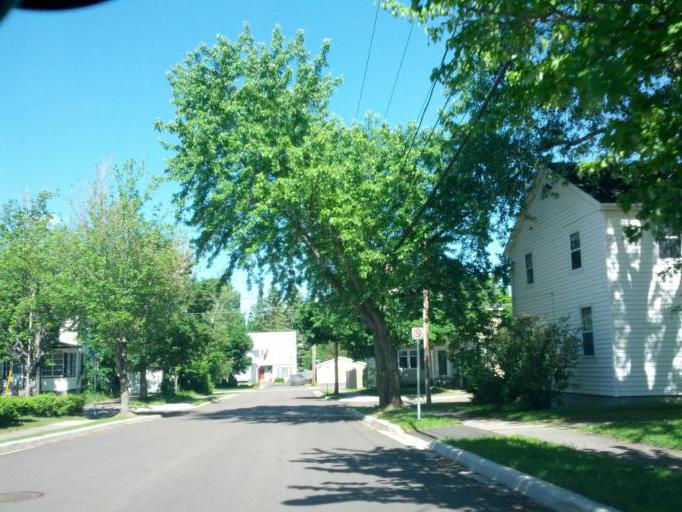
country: CA
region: New Brunswick
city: Moncton
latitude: 46.1005
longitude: -64.7942
